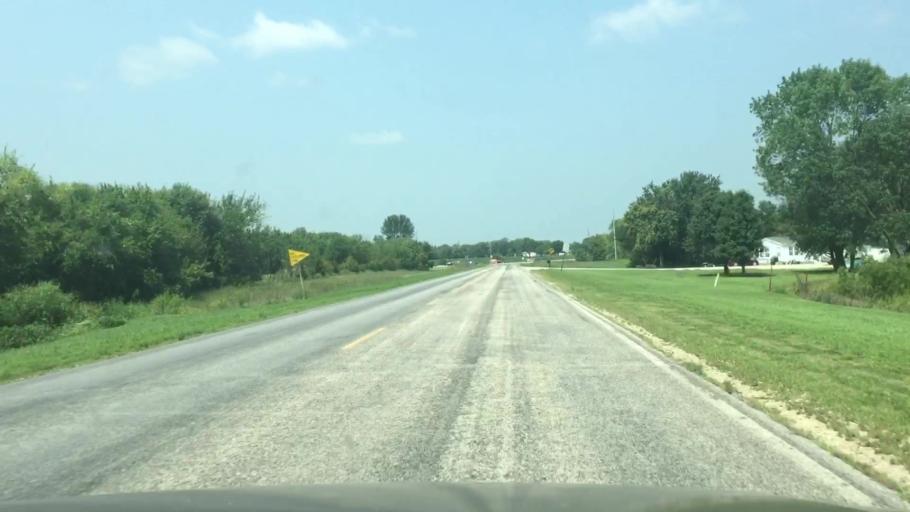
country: US
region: Kansas
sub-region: Allen County
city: Iola
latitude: 37.8879
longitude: -95.4061
